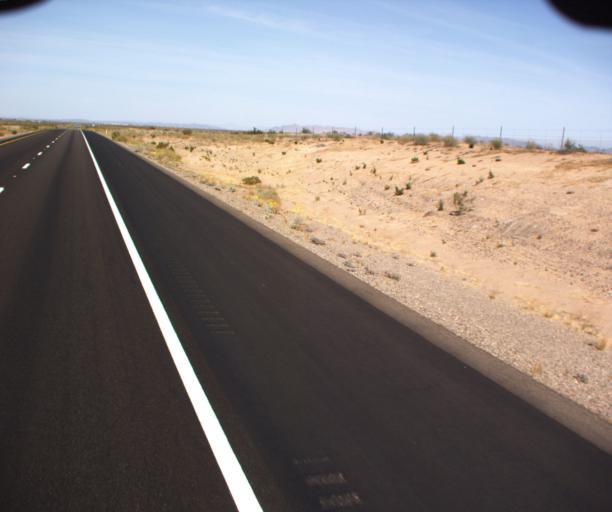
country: US
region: Arizona
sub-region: Yuma County
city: Somerton
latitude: 32.5622
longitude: -114.5603
